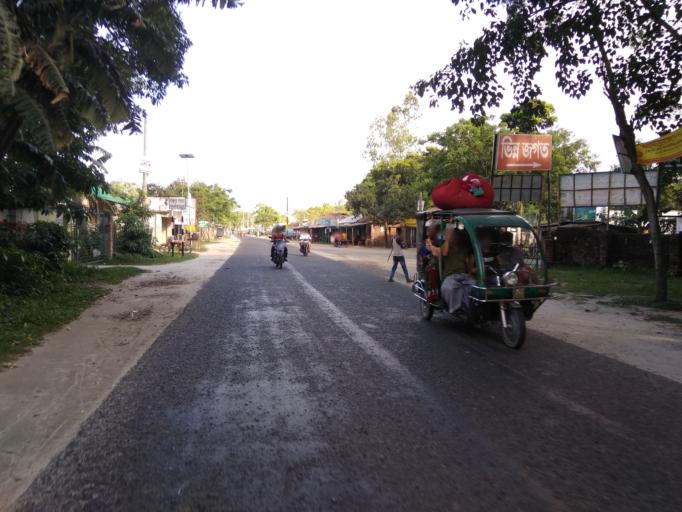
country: BD
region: Rangpur Division
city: Rangpur
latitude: 25.8303
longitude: 89.1196
